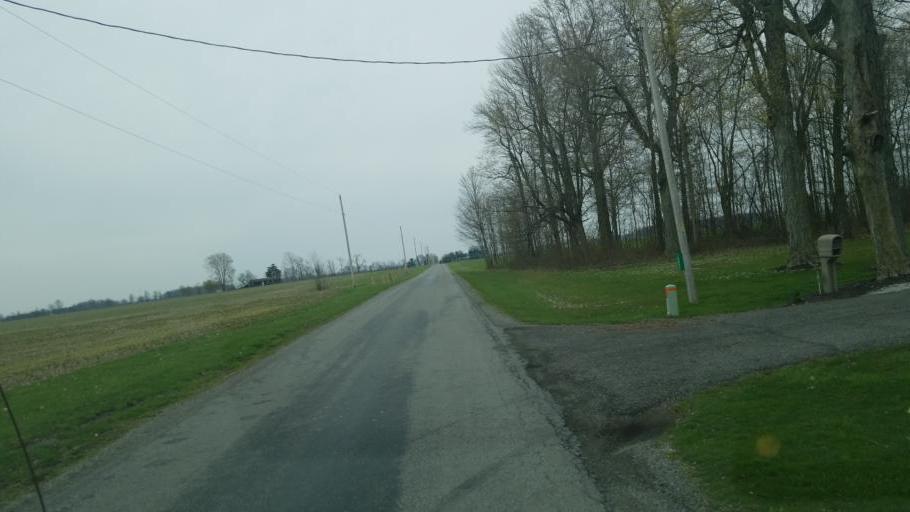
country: US
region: Ohio
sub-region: Hardin County
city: Forest
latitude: 40.8907
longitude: -83.5208
